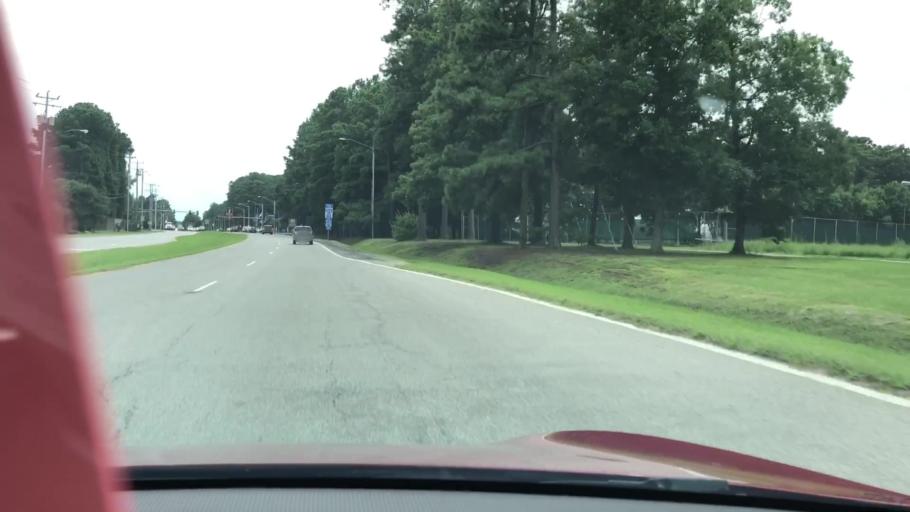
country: US
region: Virginia
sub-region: City of Virginia Beach
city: Virginia Beach
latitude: 36.8136
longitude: -75.9888
